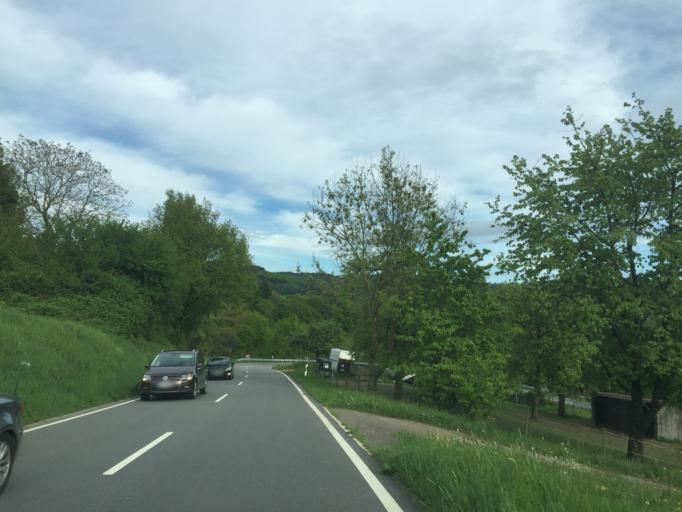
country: DE
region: Baden-Wuerttemberg
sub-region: Karlsruhe Region
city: Wilhelmsfeld
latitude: 49.4949
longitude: 8.7263
